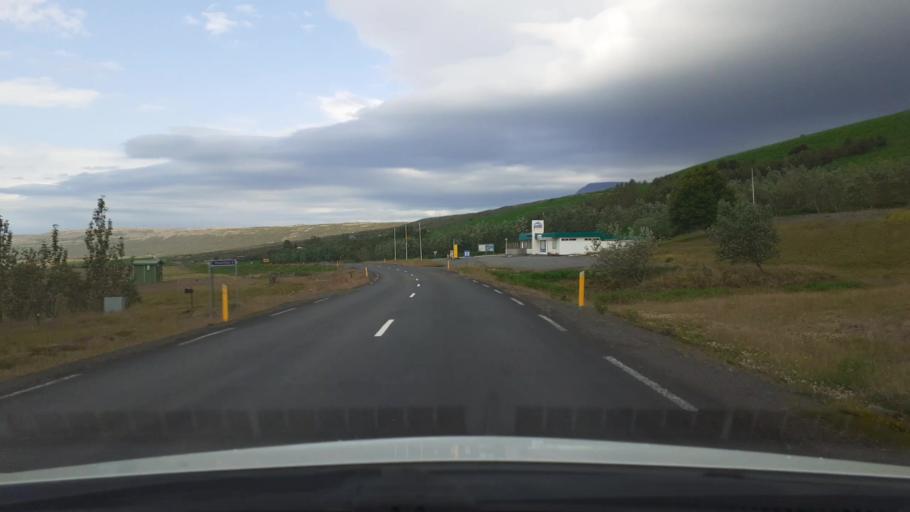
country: IS
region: Capital Region
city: Mosfellsbaer
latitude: 64.4097
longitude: -21.5954
